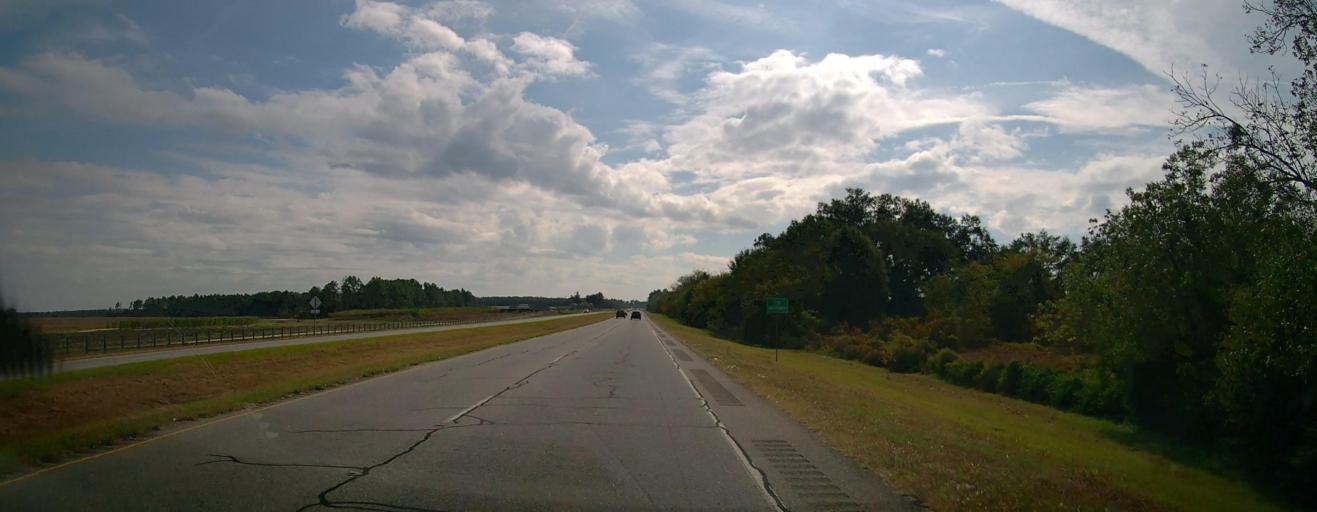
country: US
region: Georgia
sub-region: Mitchell County
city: Camilla
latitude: 31.3337
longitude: -84.1713
